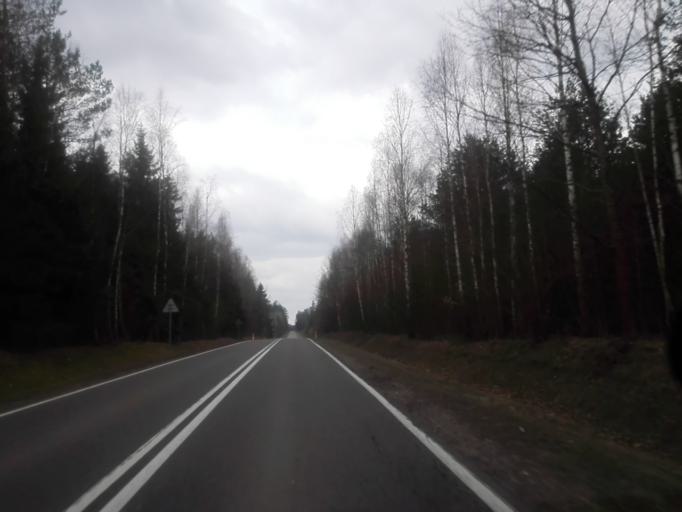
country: PL
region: Podlasie
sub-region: Powiat sejnenski
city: Sejny
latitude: 54.0078
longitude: 23.3233
